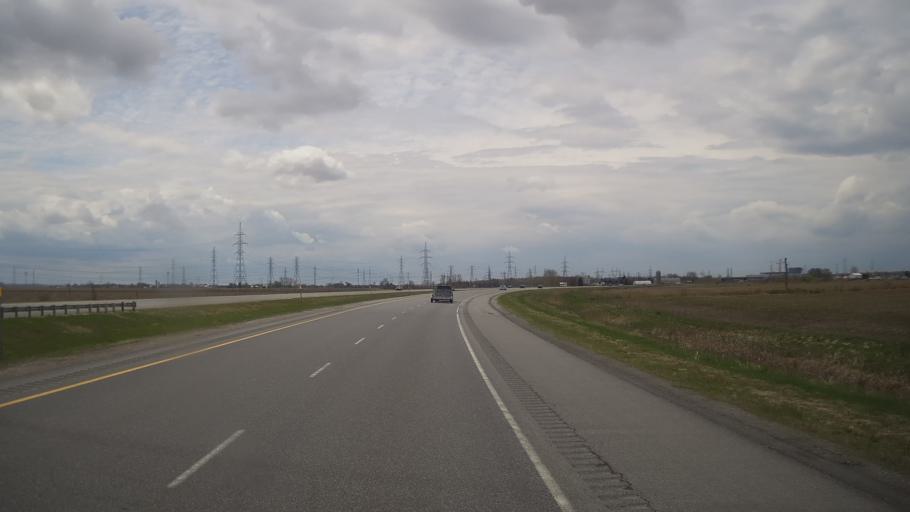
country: CA
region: Quebec
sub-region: Monteregie
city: Beauharnois
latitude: 45.2929
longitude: -73.8716
